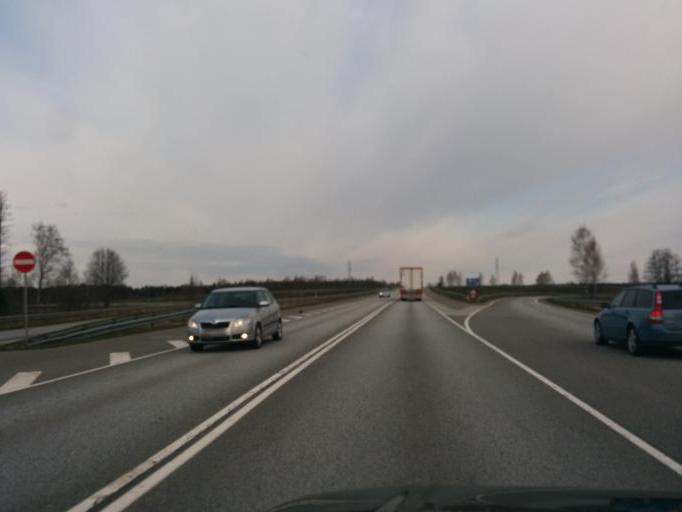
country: LV
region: Marupe
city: Marupe
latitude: 56.8320
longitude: 24.0444
